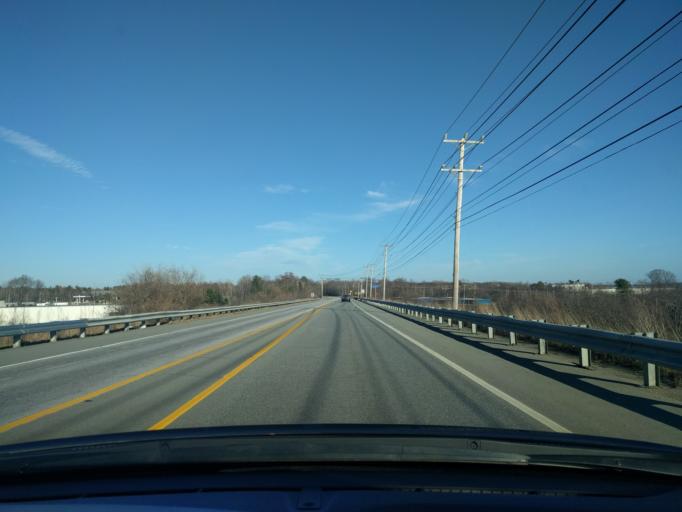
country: US
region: Maine
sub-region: Penobscot County
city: Bangor
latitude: 44.7760
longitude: -68.8012
